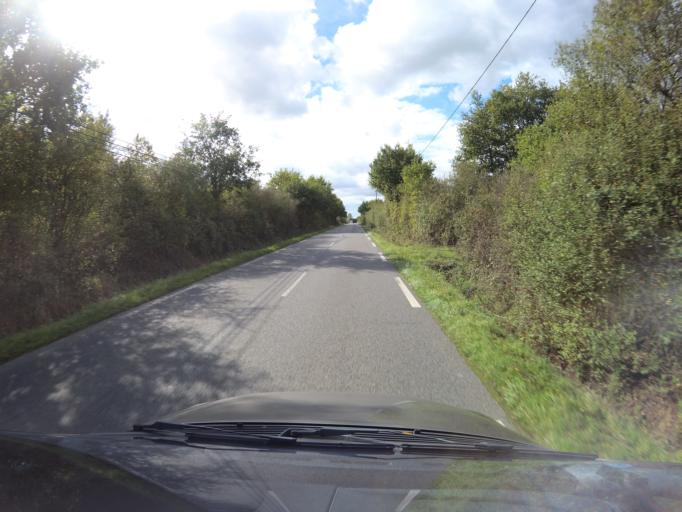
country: FR
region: Pays de la Loire
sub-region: Departement de la Loire-Atlantique
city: Heric
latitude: 47.4130
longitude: -1.6812
